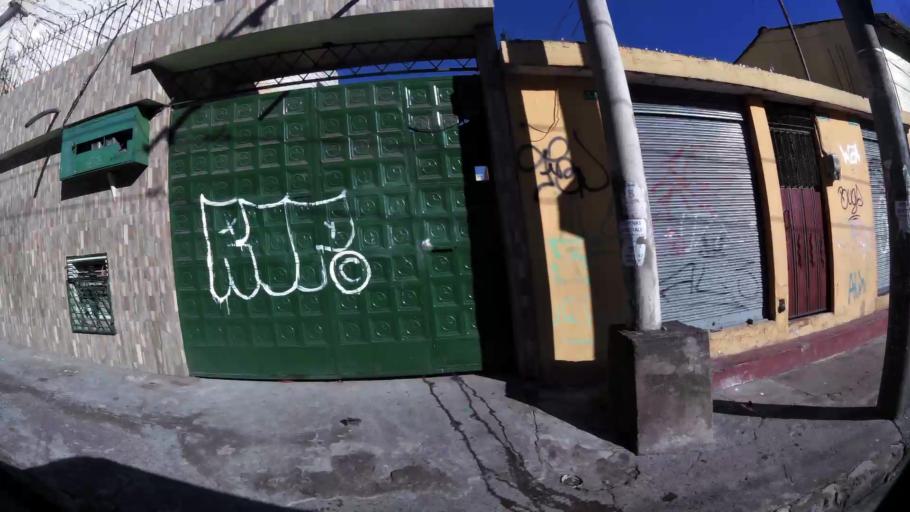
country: EC
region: Pichincha
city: Quito
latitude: -0.2403
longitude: -78.5172
